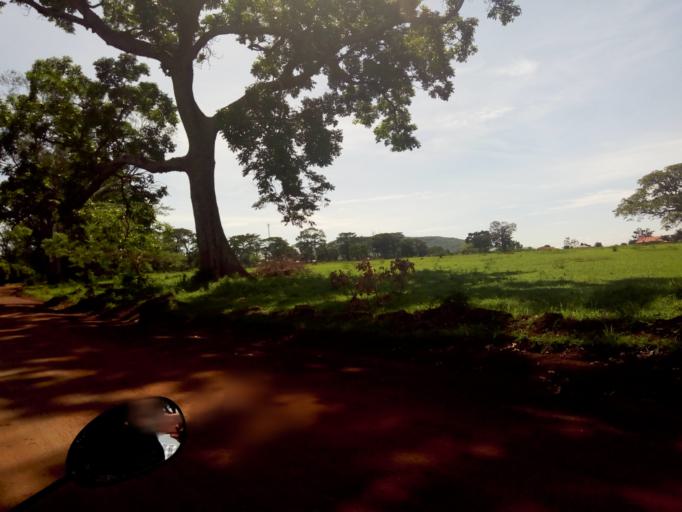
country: UG
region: Western Region
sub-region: Masindi District
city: Masindi
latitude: 1.6909
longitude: 31.7179
